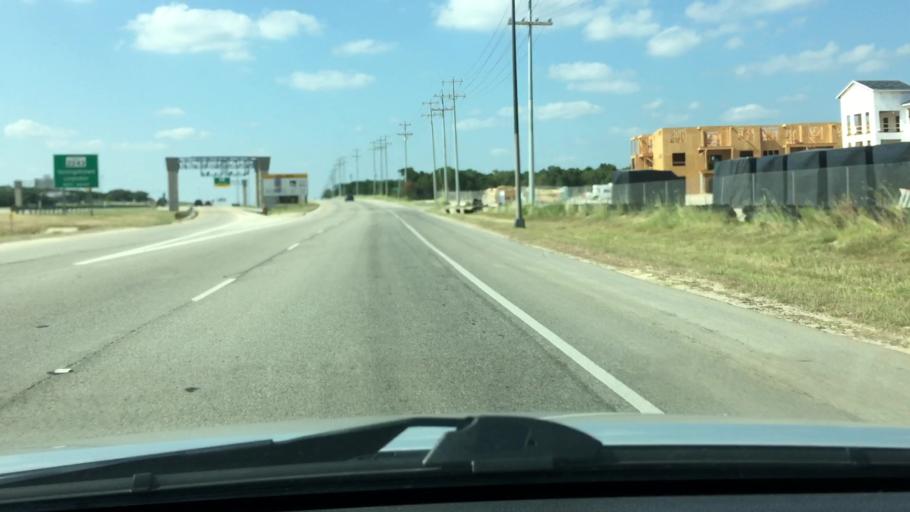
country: US
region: Texas
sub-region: Williamson County
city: Leander
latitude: 30.5675
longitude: -97.8266
